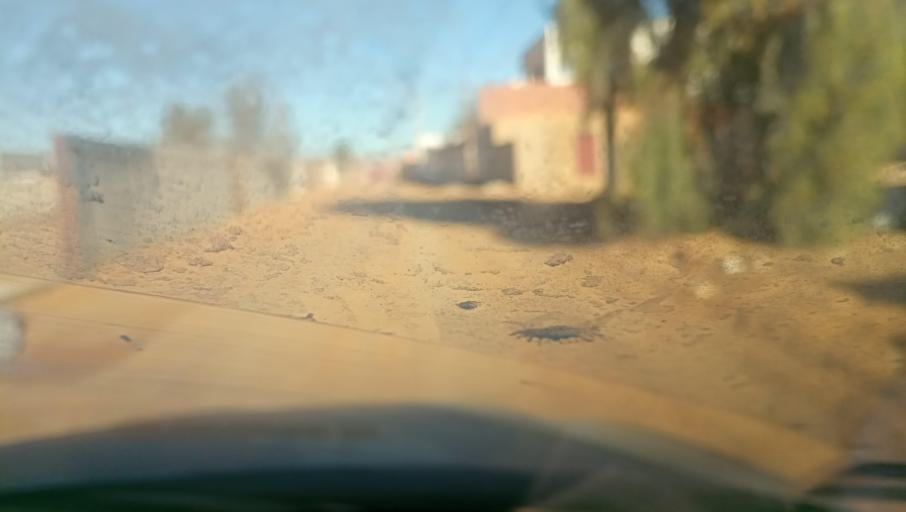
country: TN
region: Tataouine
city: Tataouine
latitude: 32.9878
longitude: 10.4586
